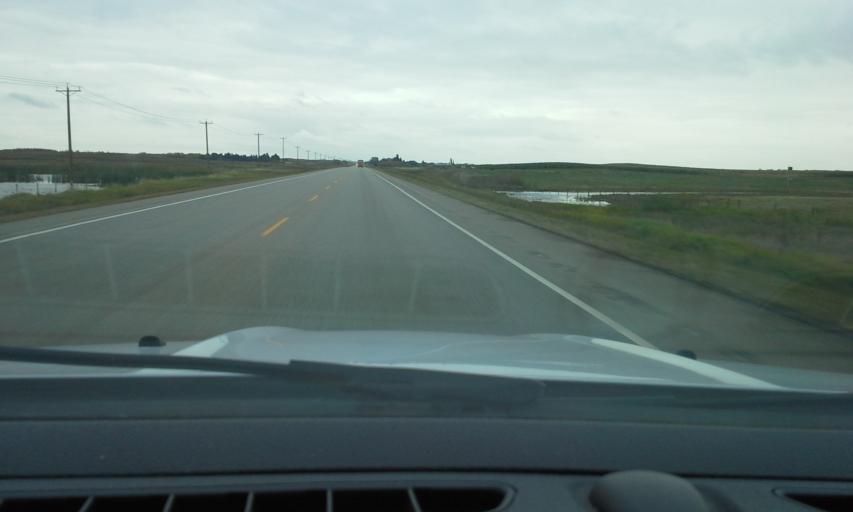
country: CA
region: Saskatchewan
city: Lloydminster
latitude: 53.2780
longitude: -109.8743
